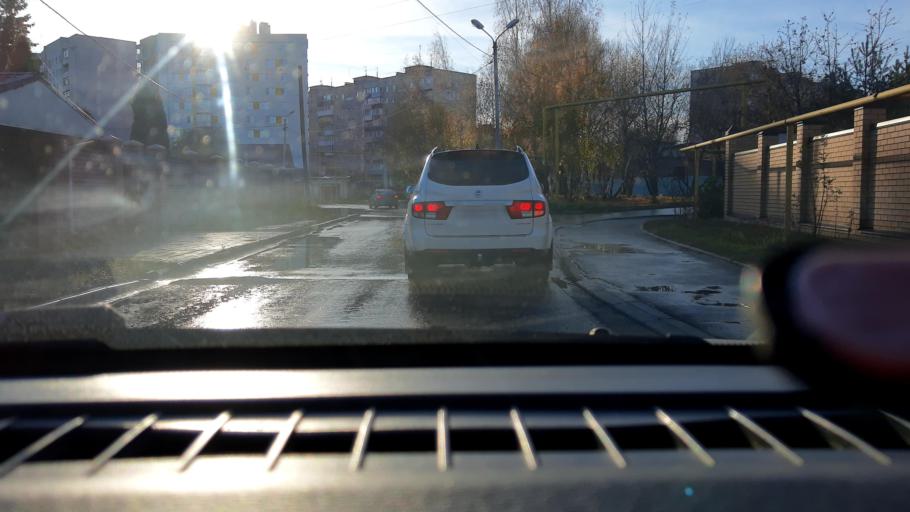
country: RU
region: Nizjnij Novgorod
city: Gorbatovka
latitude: 56.3795
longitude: 43.7995
